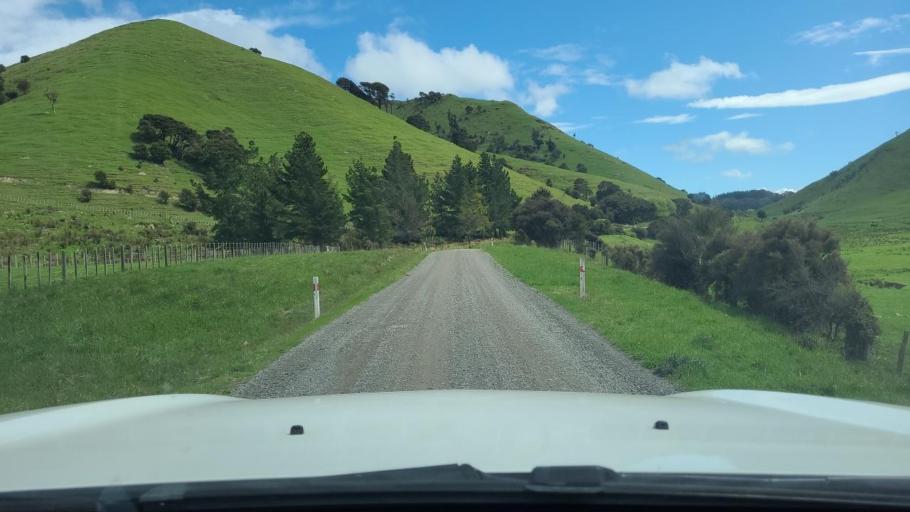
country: NZ
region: Wellington
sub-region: South Wairarapa District
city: Waipawa
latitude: -41.3259
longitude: 175.3934
